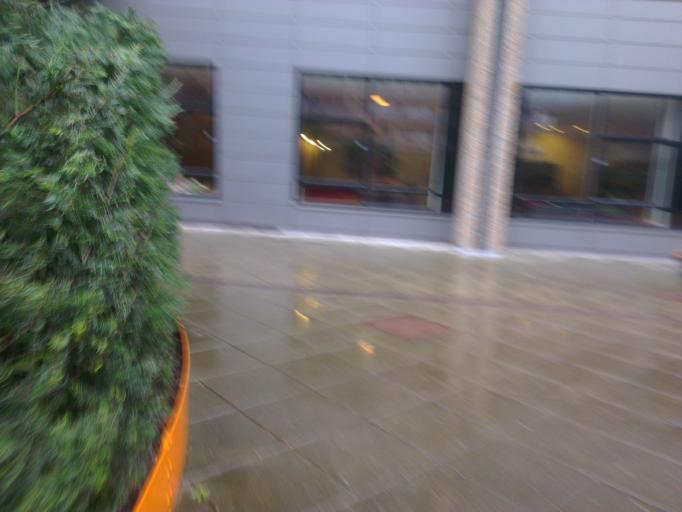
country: DK
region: Capital Region
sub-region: Kobenhavn
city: Copenhagen
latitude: 55.6961
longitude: 12.5656
